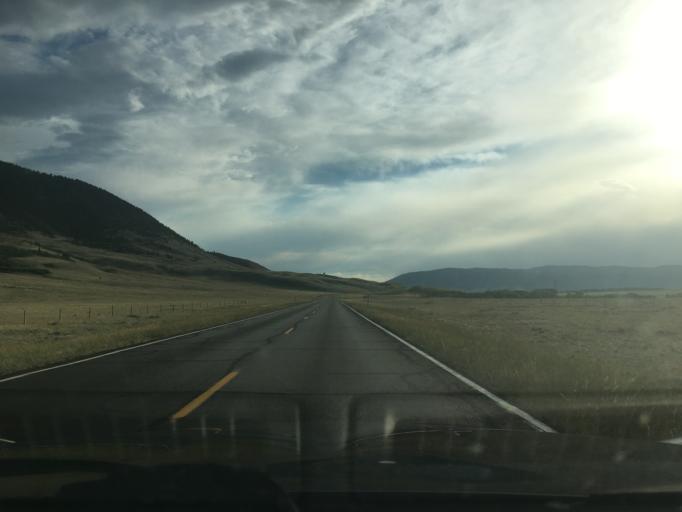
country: US
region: Wyoming
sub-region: Albany County
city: Laramie
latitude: 41.2893
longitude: -106.0341
